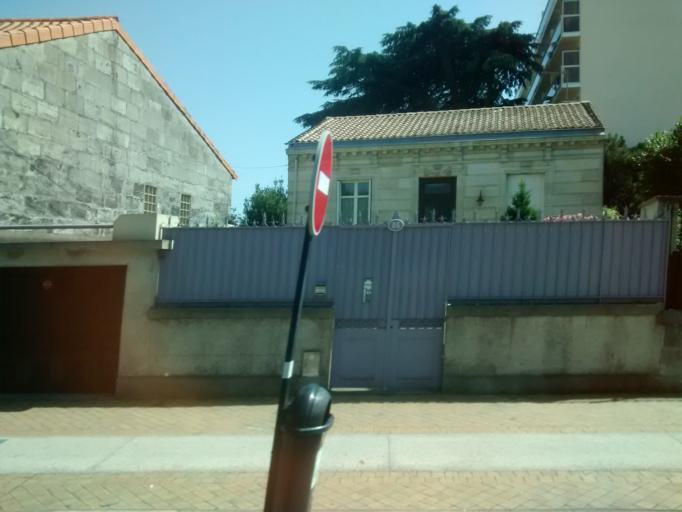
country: FR
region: Aquitaine
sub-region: Departement de la Gironde
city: Bordeaux
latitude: 44.8398
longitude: -0.6042
